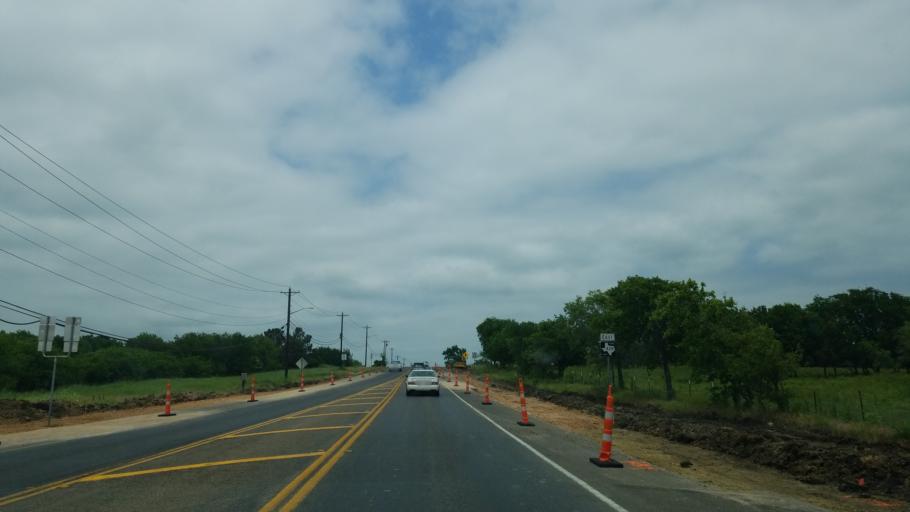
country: US
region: Texas
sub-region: Denton County
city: Denton
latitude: 33.2586
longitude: -97.1093
